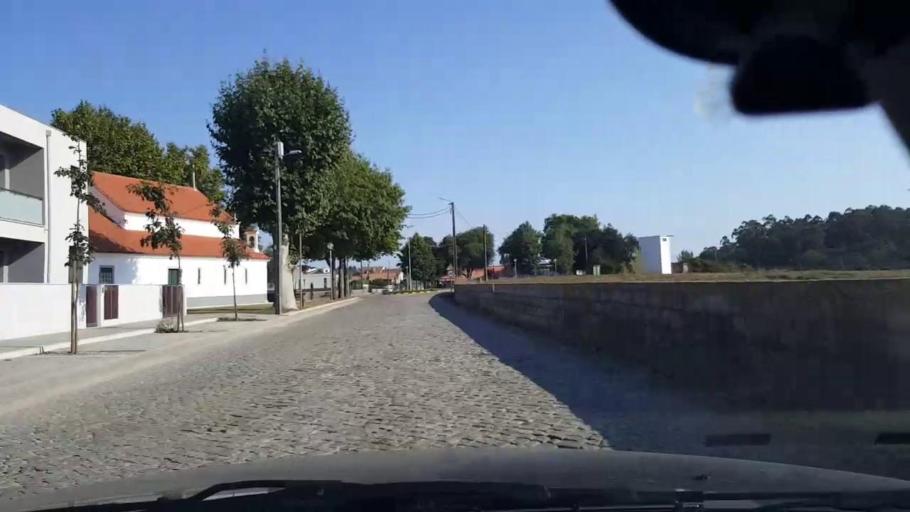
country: PT
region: Porto
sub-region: Vila do Conde
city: Arvore
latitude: 41.3513
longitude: -8.7192
